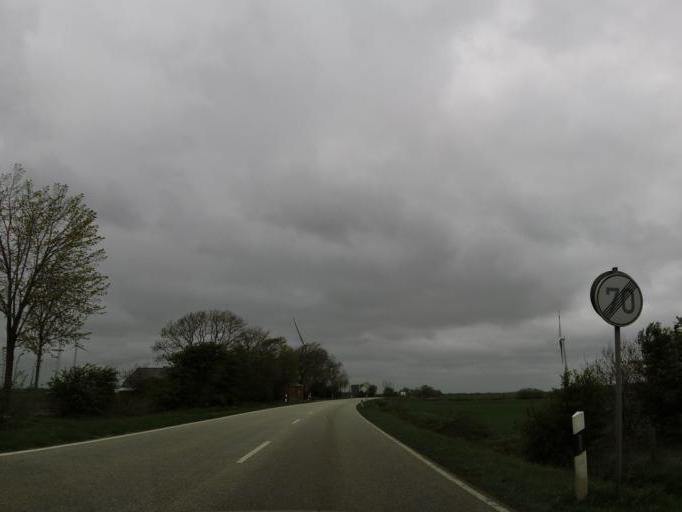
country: DE
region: Schleswig-Holstein
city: Suderlugum
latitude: 54.8872
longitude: 8.9085
